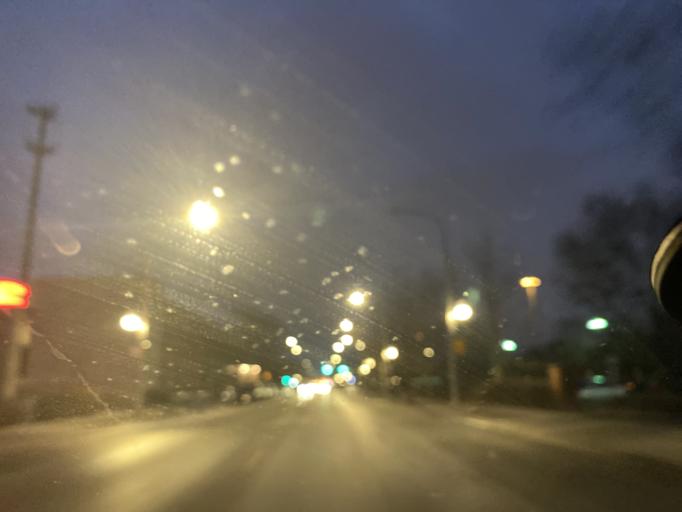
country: US
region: Illinois
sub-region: Cook County
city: Chicago
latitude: 41.7795
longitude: -87.6610
